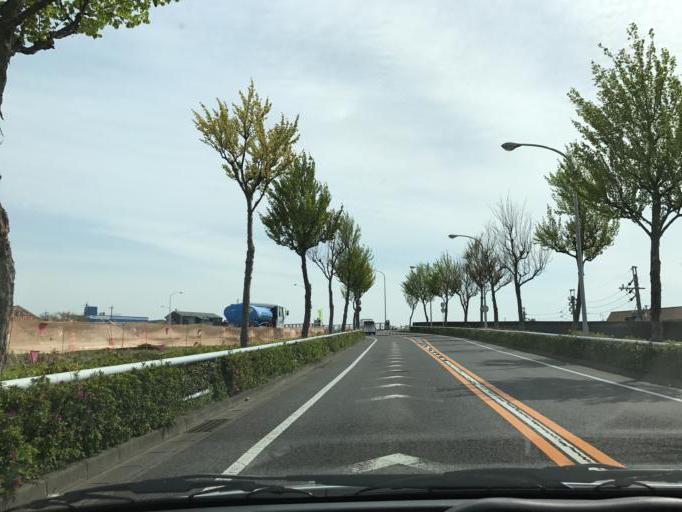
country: JP
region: Aichi
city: Nagoya-shi
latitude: 35.1163
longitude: 136.9615
